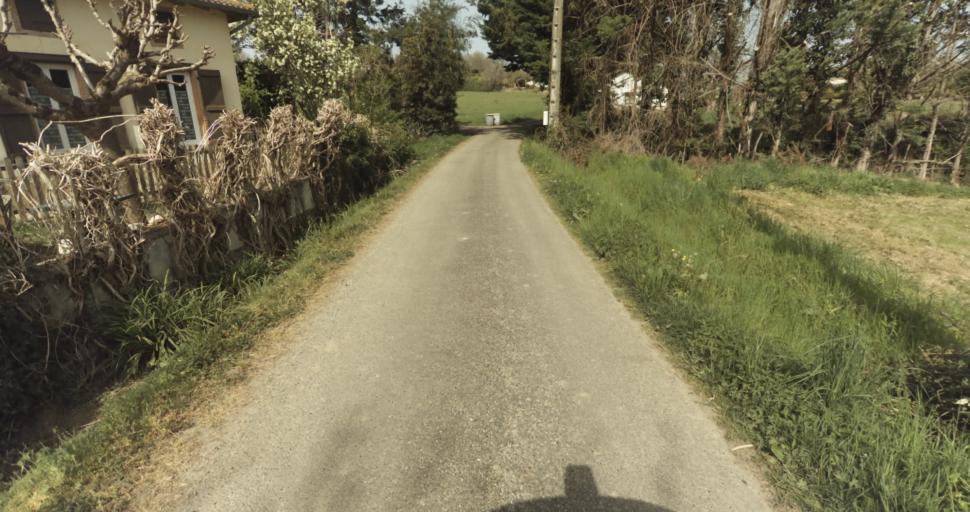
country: FR
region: Midi-Pyrenees
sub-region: Departement du Tarn-et-Garonne
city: Moissac
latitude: 44.1292
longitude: 1.1544
